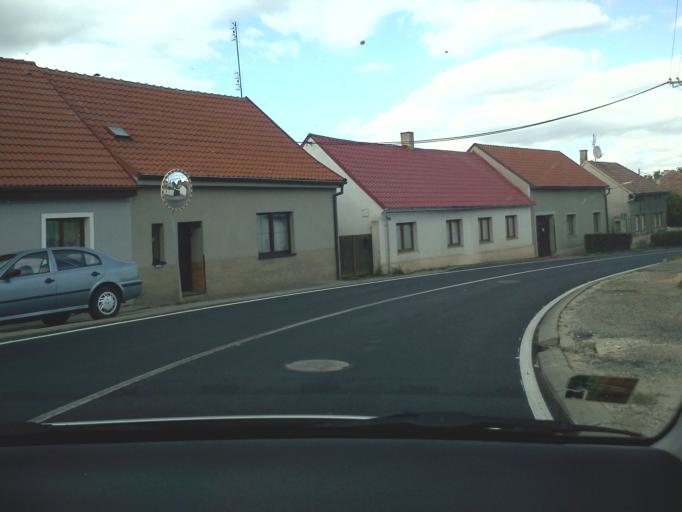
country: CZ
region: Central Bohemia
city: Cesky Brod
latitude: 50.1059
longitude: 14.8551
